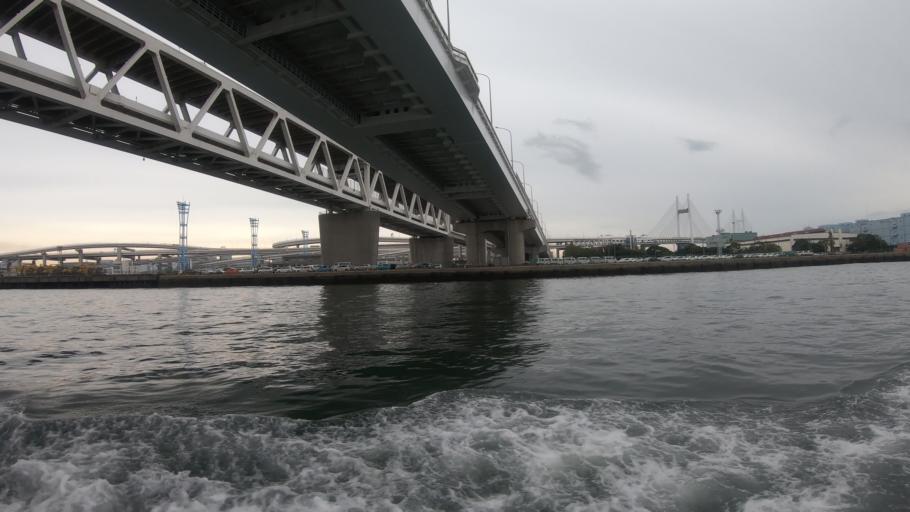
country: JP
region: Kanagawa
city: Yokohama
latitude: 35.4676
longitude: 139.6761
